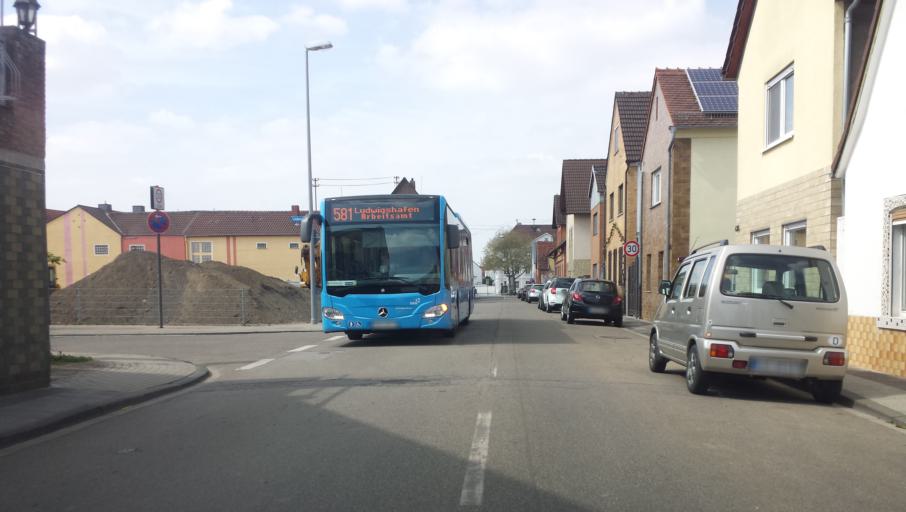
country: DE
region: Rheinland-Pfalz
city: Gartenstadt
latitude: 49.4552
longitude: 8.3855
